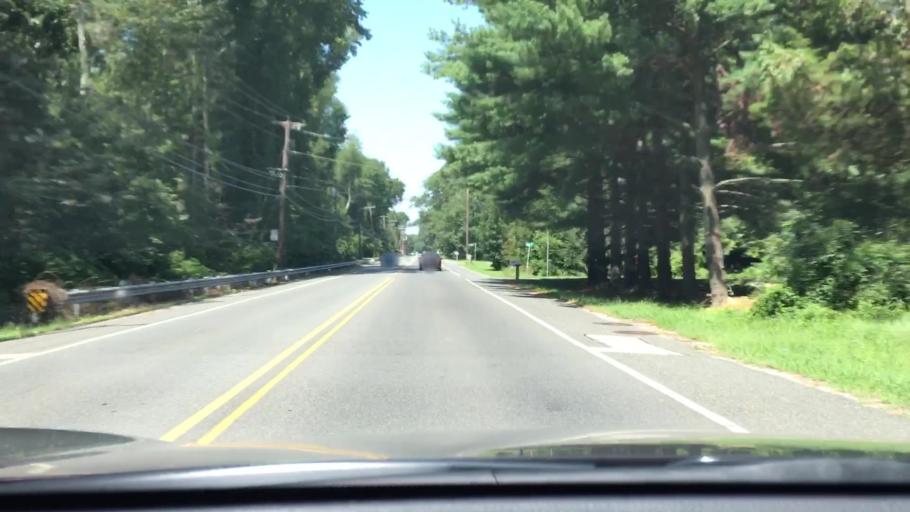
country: US
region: New Jersey
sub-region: Cumberland County
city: Laurel Lake
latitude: 39.3364
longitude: -75.0244
